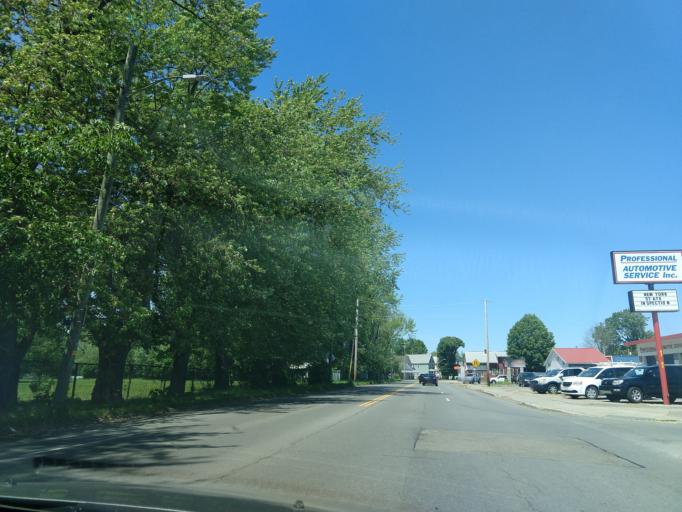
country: US
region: New York
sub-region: Erie County
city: West Seneca
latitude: 42.8457
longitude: -78.7974
